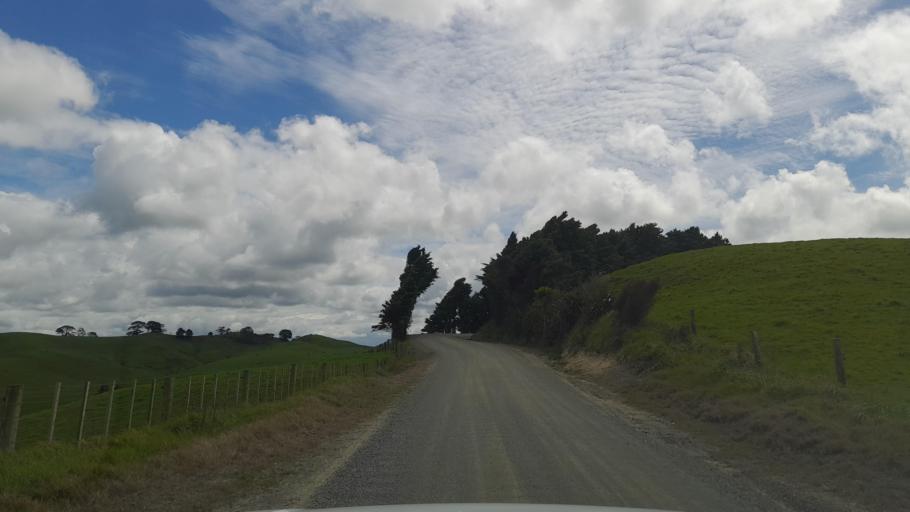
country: NZ
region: Auckland
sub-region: Auckland
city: Wellsford
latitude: -36.1895
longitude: 174.3395
